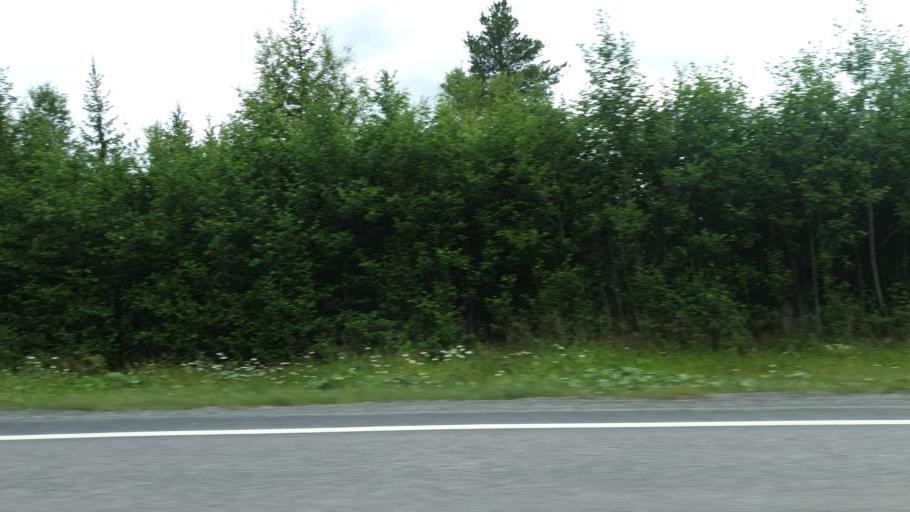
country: NO
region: Sor-Trondelag
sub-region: Rennebu
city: Berkak
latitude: 62.7958
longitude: 10.0179
